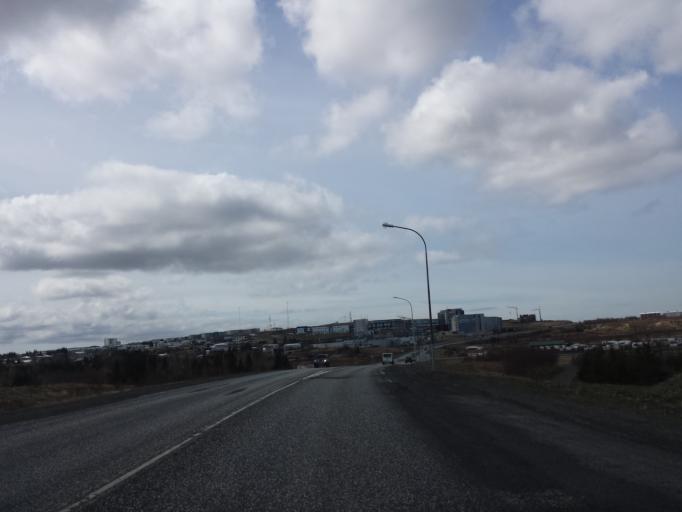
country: IS
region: Capital Region
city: Mosfellsbaer
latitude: 64.0981
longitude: -21.7875
